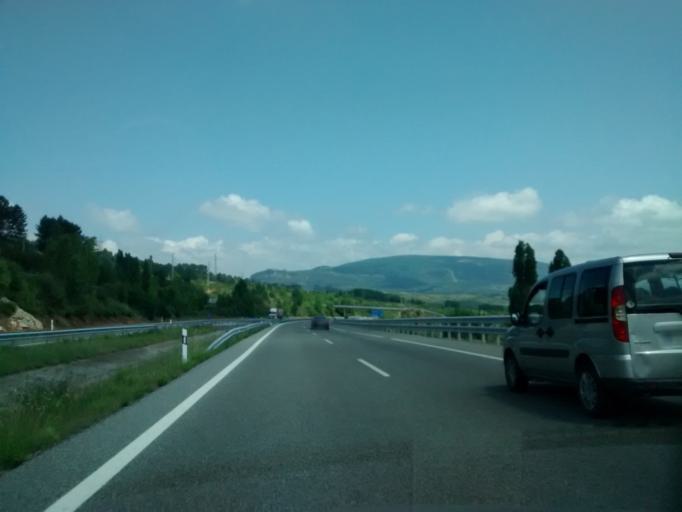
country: ES
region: Castille and Leon
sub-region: Provincia de Leon
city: Congosto
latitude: 42.5808
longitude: -6.5293
